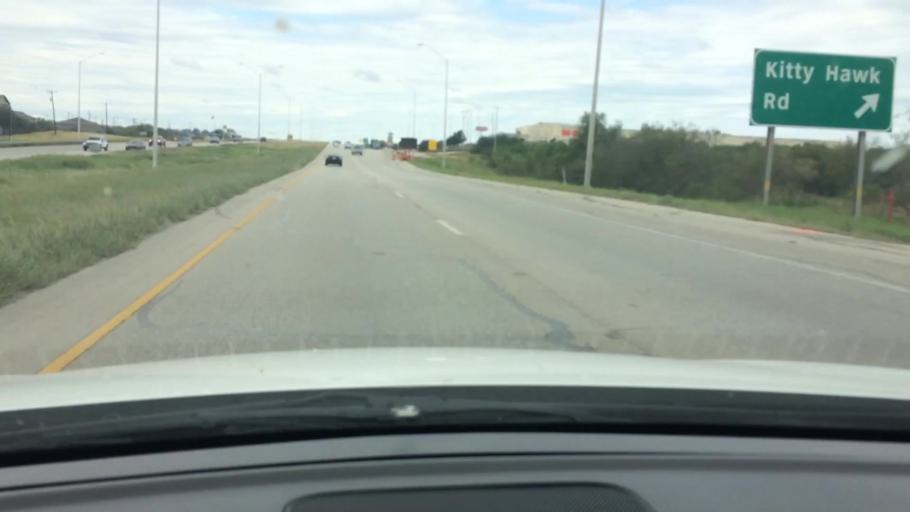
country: US
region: Texas
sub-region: Bexar County
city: Universal City
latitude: 29.5433
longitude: -98.3106
